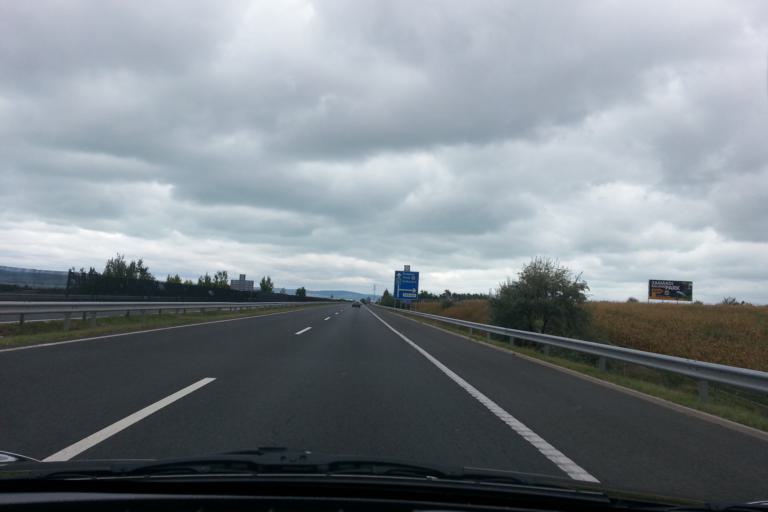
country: HU
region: Somogy
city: Zamardi
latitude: 46.8696
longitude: 17.9673
